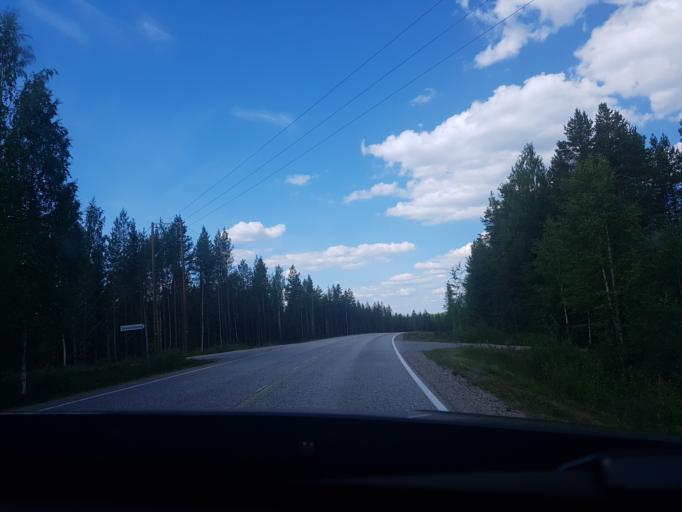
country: FI
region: Kainuu
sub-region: Kehys-Kainuu
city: Kuhmo
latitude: 64.2440
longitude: 29.8086
